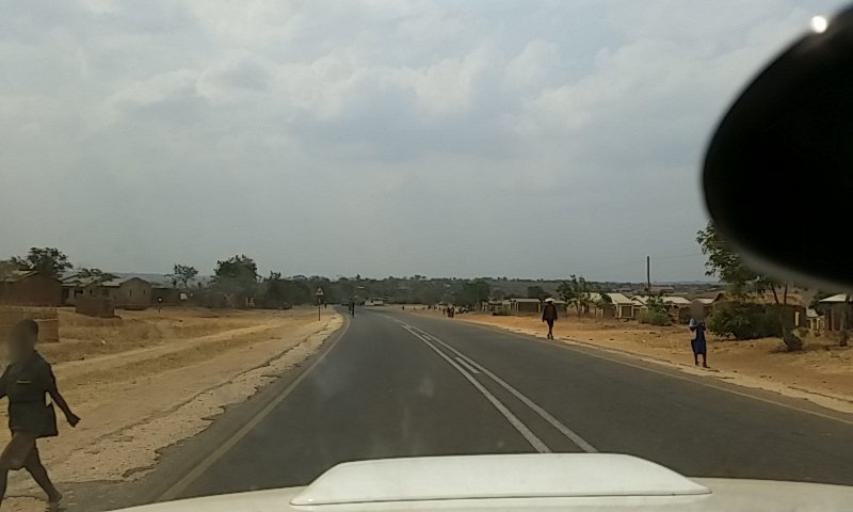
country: MW
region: Central Region
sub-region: Lilongwe District
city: Lilongwe
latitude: -13.8579
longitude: 33.8325
